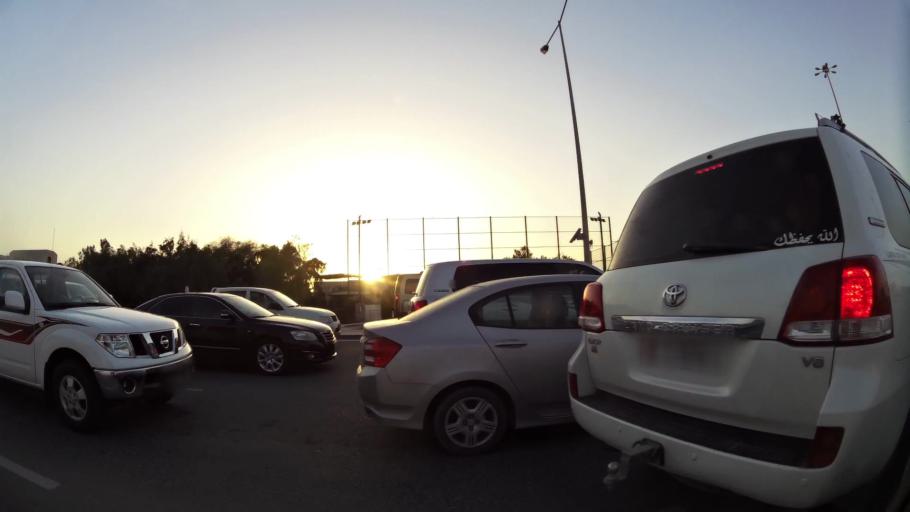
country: QA
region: Baladiyat ar Rayyan
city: Ar Rayyan
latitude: 25.3265
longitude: 51.4612
